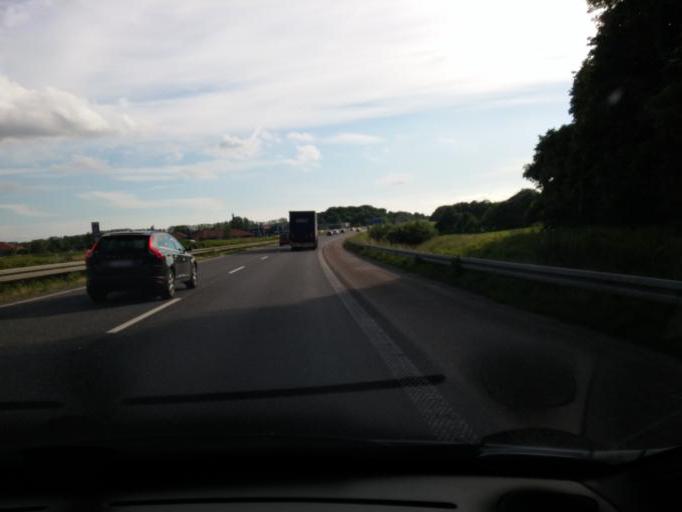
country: DK
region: Zealand
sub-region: Slagelse Kommune
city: Slagelse
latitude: 55.3906
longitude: 11.3653
